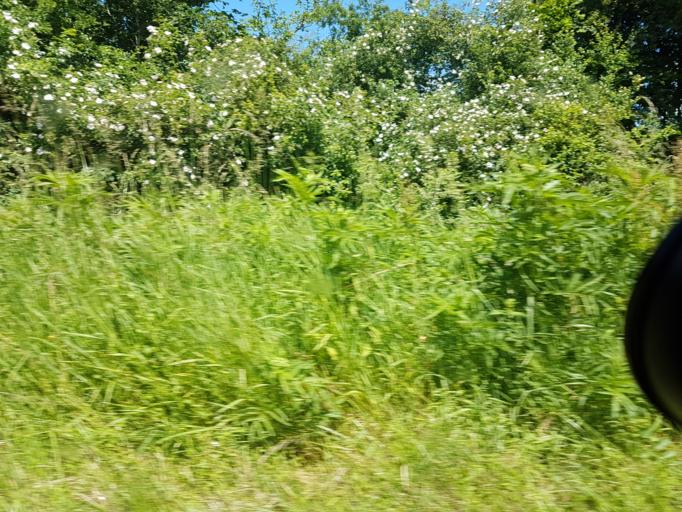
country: FR
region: Bourgogne
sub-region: Departement de Saone-et-Loire
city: Curgy
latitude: 47.0286
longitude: 4.4258
